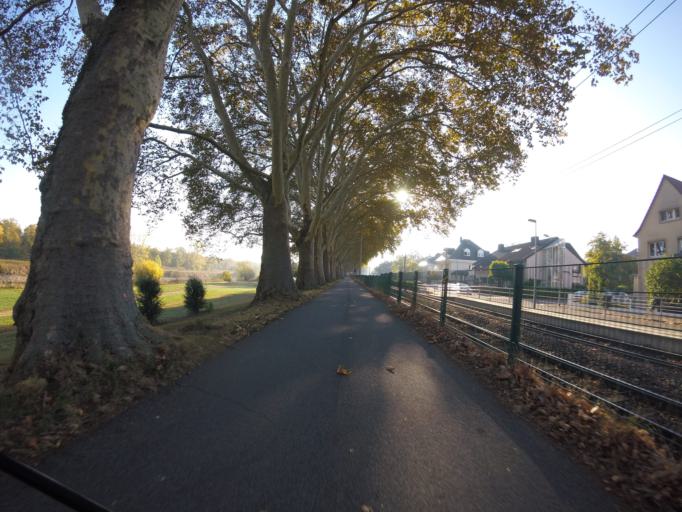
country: DE
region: Baden-Wuerttemberg
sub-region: Karlsruhe Region
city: Mannheim
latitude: 49.4811
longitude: 8.5132
